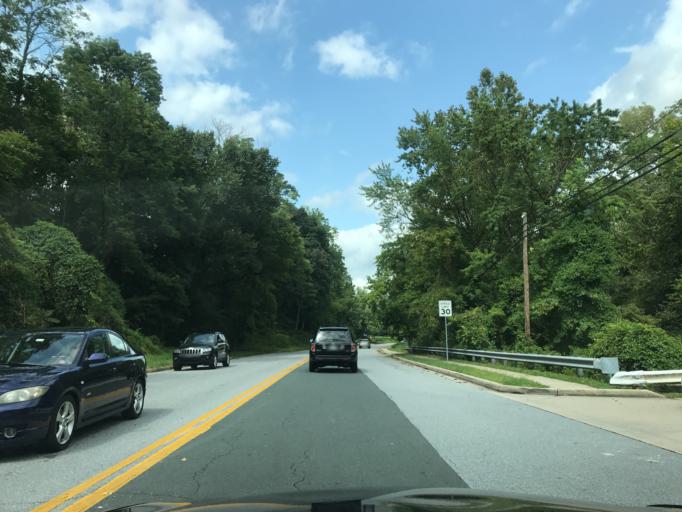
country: US
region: Maryland
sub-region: Baltimore County
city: Mays Chapel
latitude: 39.4094
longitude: -76.6488
